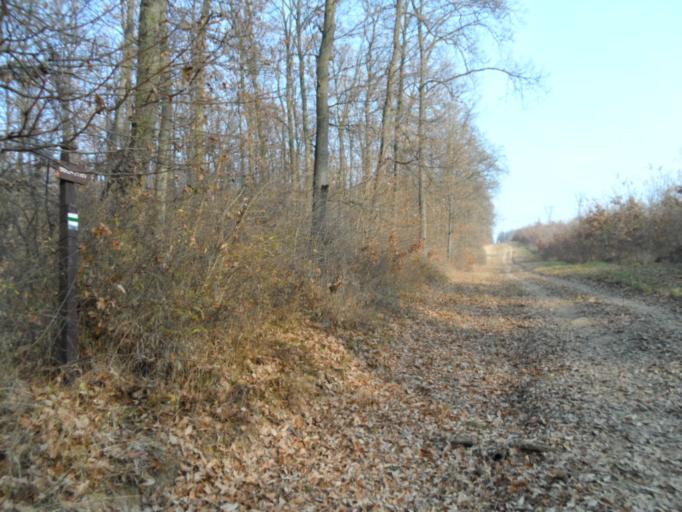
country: HU
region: Somogy
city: Siofok
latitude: 46.8357
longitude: 18.0260
